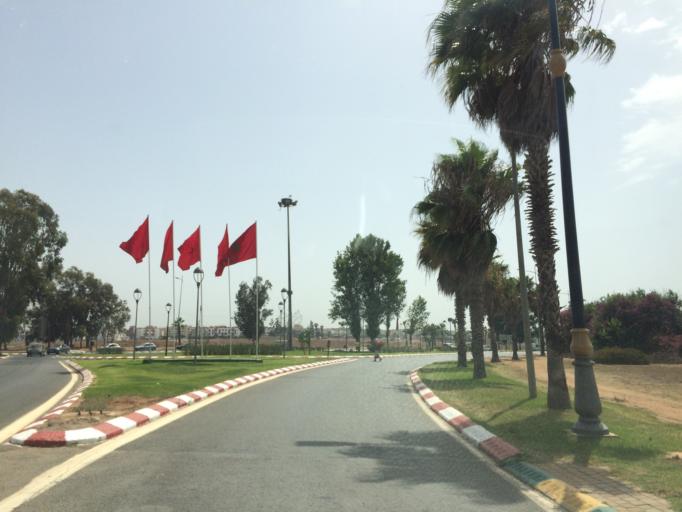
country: MA
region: Rabat-Sale-Zemmour-Zaer
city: Sale
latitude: 34.0319
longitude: -6.7534
